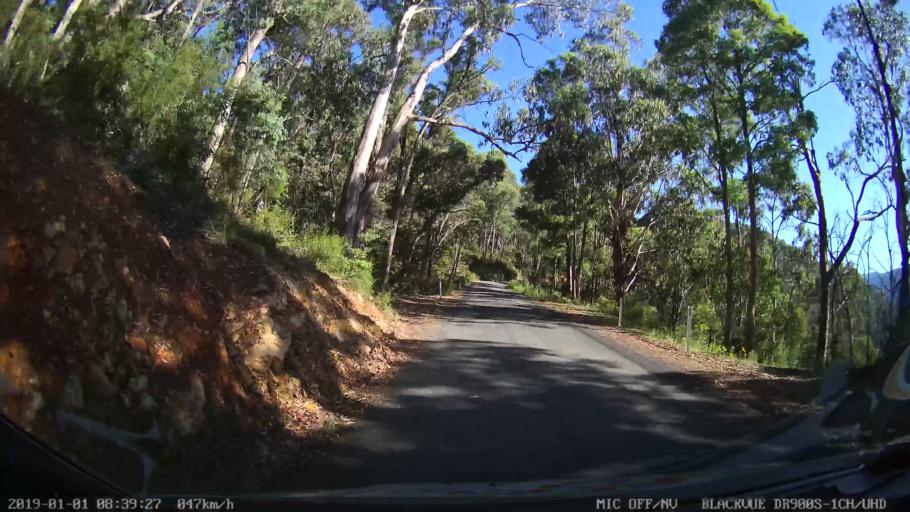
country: AU
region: New South Wales
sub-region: Snowy River
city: Jindabyne
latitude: -36.3313
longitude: 148.1931
